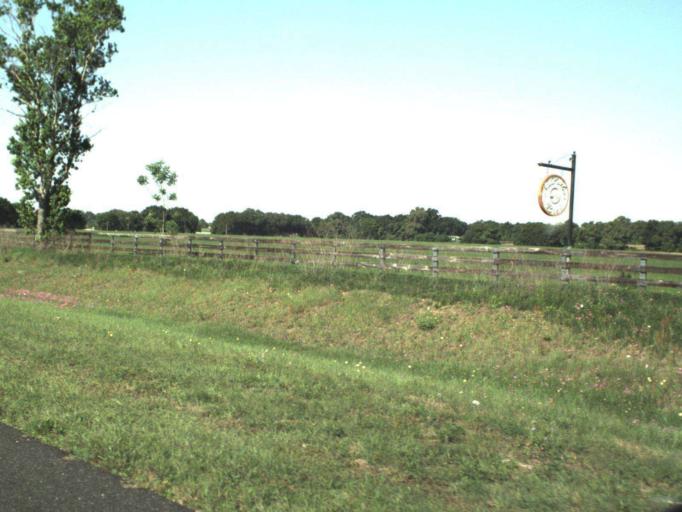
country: US
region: Florida
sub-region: Marion County
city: Citra
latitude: 29.3593
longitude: -82.1405
